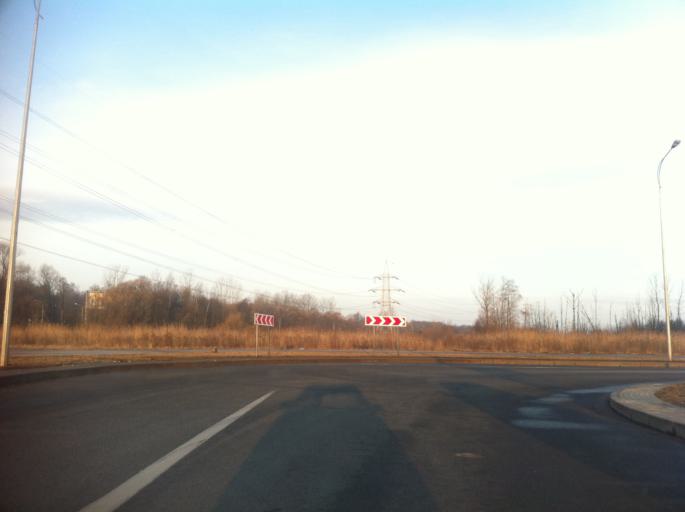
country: RU
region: St.-Petersburg
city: Sosnovaya Polyana
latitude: 59.8481
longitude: 30.1337
